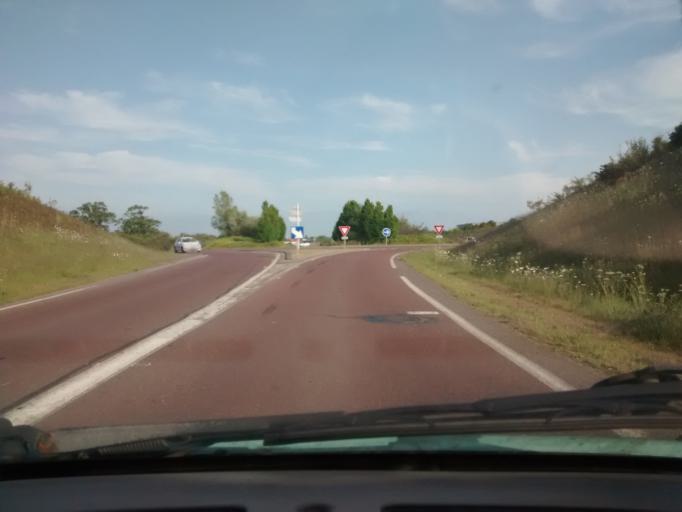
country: FR
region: Lower Normandy
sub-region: Departement de la Manche
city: Pont-Hebert
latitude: 49.1351
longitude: -1.1761
